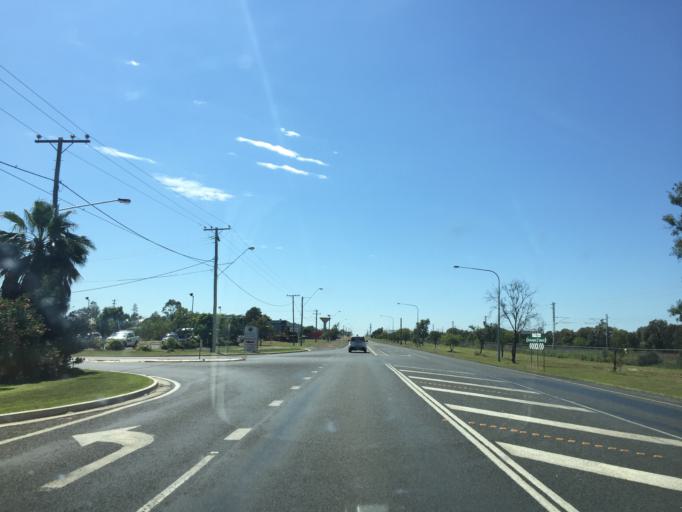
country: AU
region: Queensland
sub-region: Central Highlands
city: Blackwater
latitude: -23.5858
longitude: 148.8720
